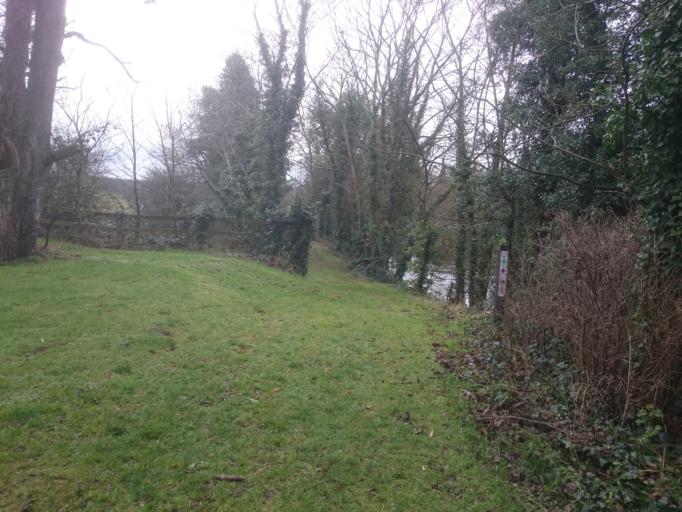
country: IE
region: Leinster
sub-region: Laois
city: Abbeyleix
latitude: 52.8476
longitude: -7.4028
